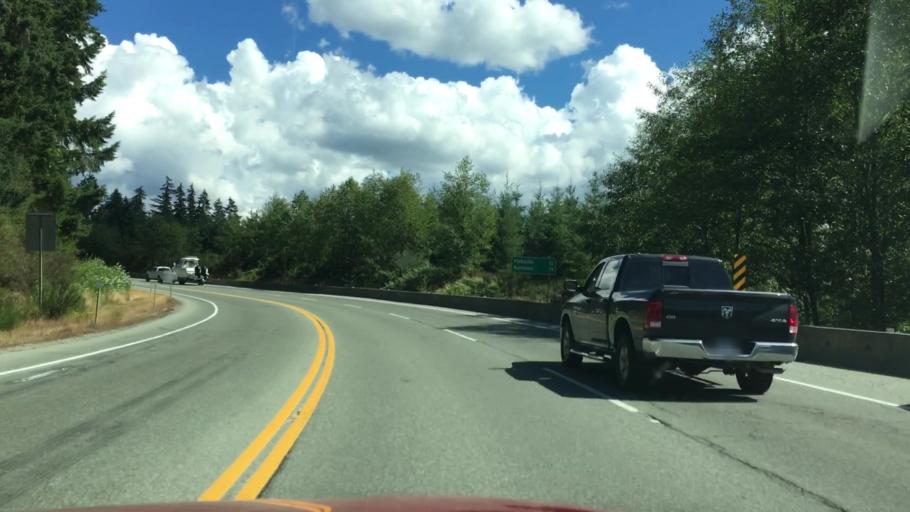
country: CA
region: British Columbia
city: Port Alberni
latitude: 49.2651
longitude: -124.7455
